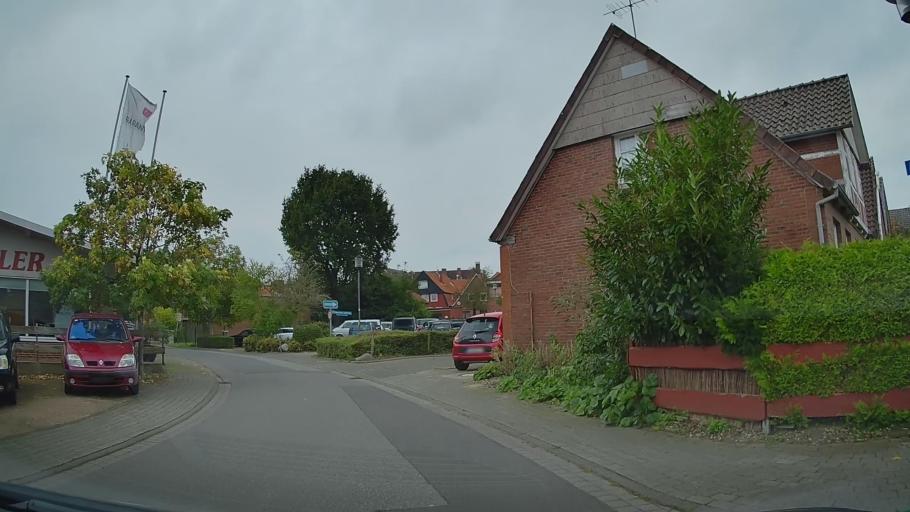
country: DE
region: Lower Saxony
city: Freiburg
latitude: 53.8247
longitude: 9.2883
